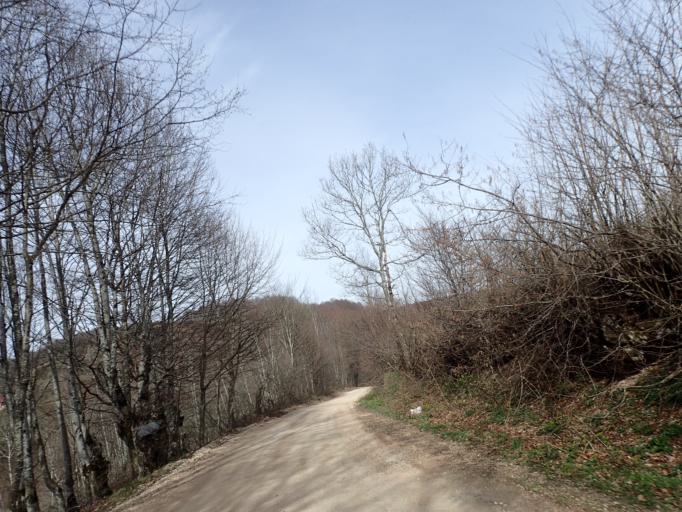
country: TR
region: Ordu
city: Kumru
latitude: 40.8054
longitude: 37.1763
